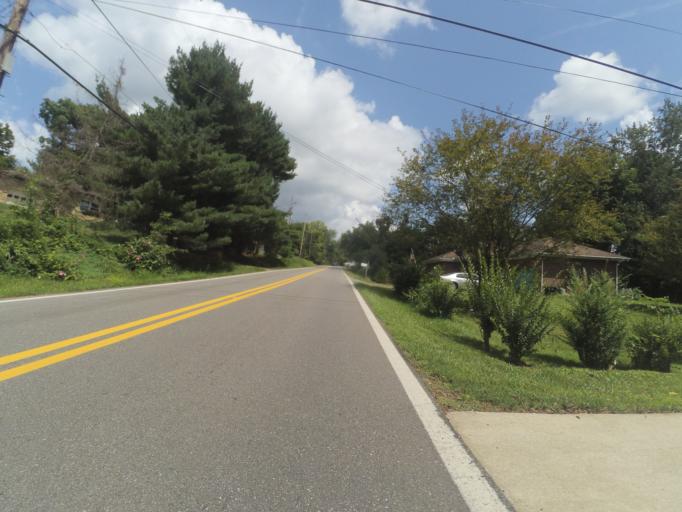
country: US
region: West Virginia
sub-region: Cabell County
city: Pea Ridge
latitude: 38.4120
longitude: -82.3542
